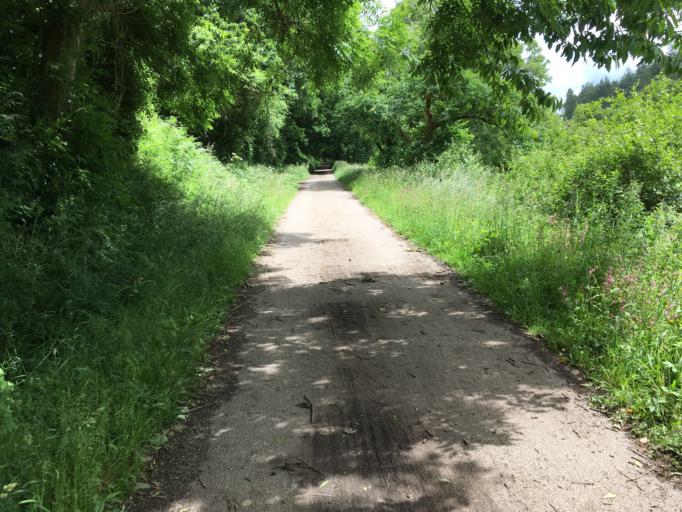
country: GB
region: England
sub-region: Cornwall
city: Wadebridge
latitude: 50.4995
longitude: -4.8092
